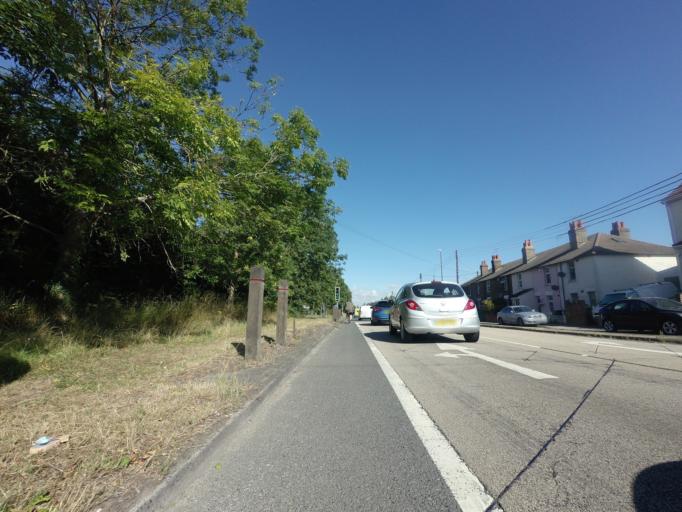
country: GB
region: England
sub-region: Medway
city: Cuxton
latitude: 51.4133
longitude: 0.4539
